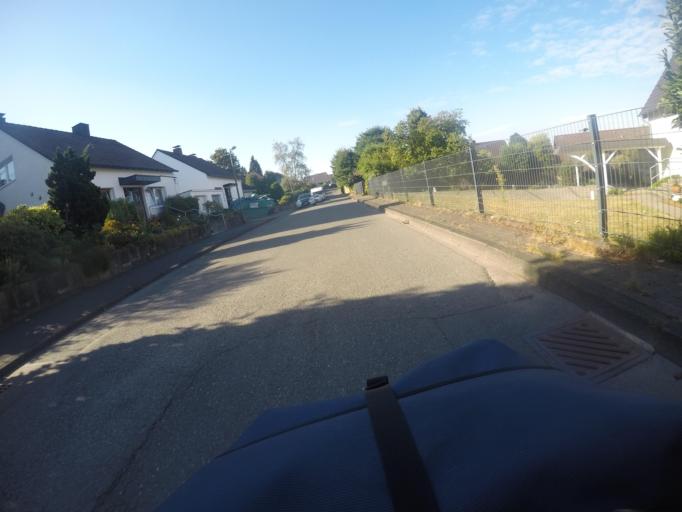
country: DE
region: North Rhine-Westphalia
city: Haan
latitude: 51.2143
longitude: 7.0436
